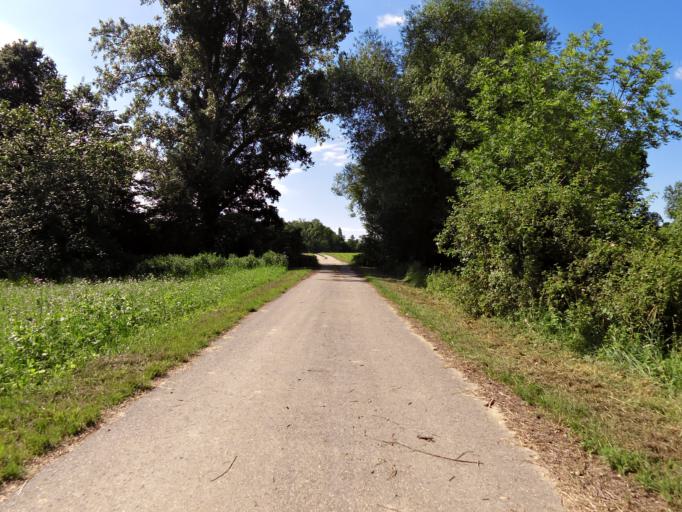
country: DE
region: Rheinland-Pfalz
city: Altdorf
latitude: 49.2818
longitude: 8.1996
